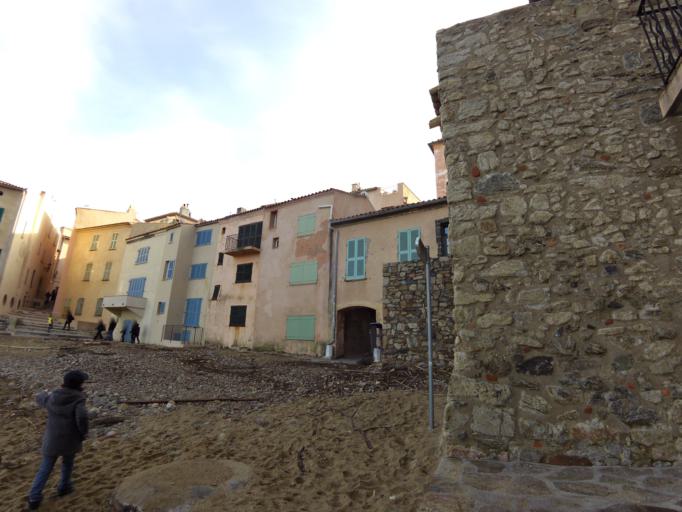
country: FR
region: Provence-Alpes-Cote d'Azur
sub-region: Departement du Var
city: Saint-Tropez
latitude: 43.2736
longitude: 6.6396
